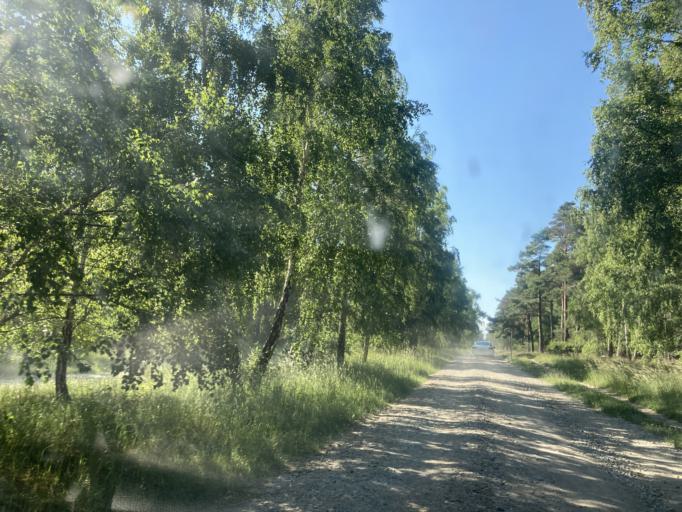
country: DK
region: Capital Region
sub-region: Halsnaes Kommune
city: Frederiksvaerk
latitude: 56.0149
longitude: 12.0155
